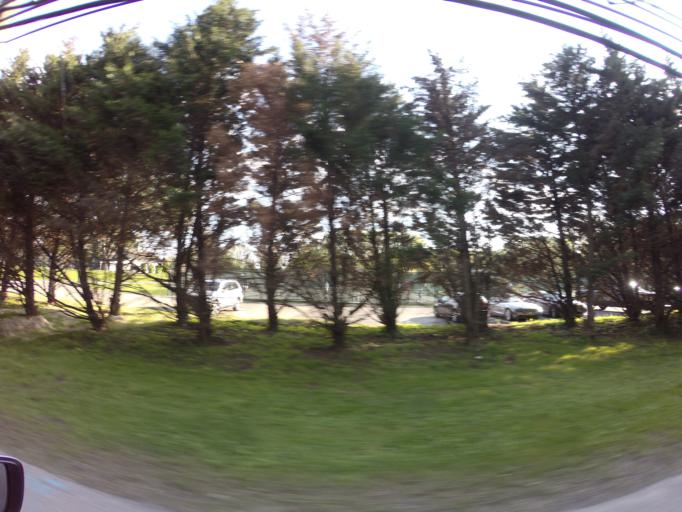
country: US
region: Maryland
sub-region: Baltimore County
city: Mays Chapel
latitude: 39.4155
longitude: -76.6627
